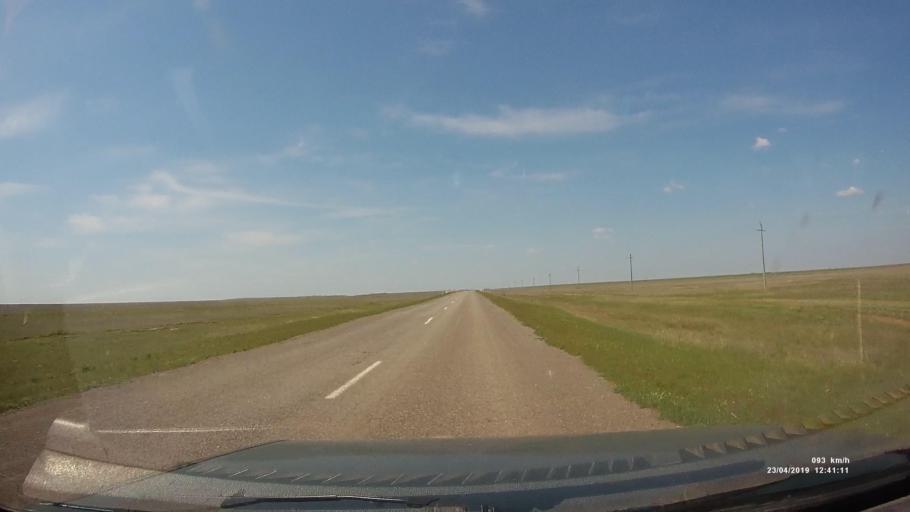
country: RU
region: Kalmykiya
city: Yashalta
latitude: 46.4462
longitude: 42.6849
